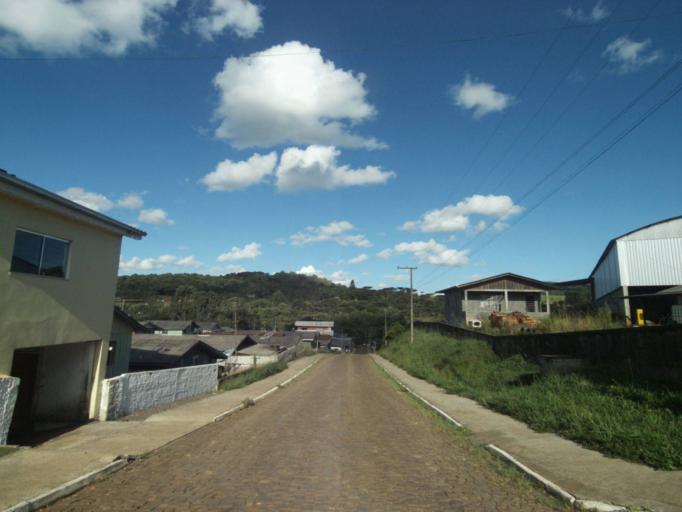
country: BR
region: Parana
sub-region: Uniao Da Vitoria
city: Uniao da Vitoria
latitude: -26.1605
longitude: -51.5348
